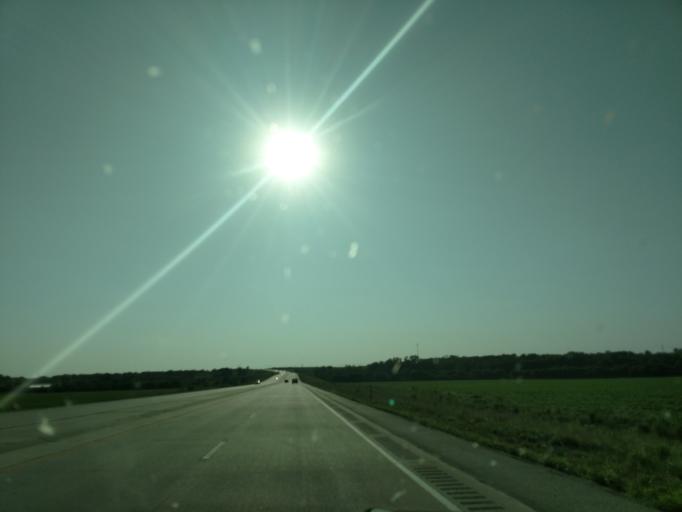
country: US
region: Nebraska
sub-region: Sarpy County
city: Offutt Air Force Base
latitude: 41.0803
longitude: -95.9095
